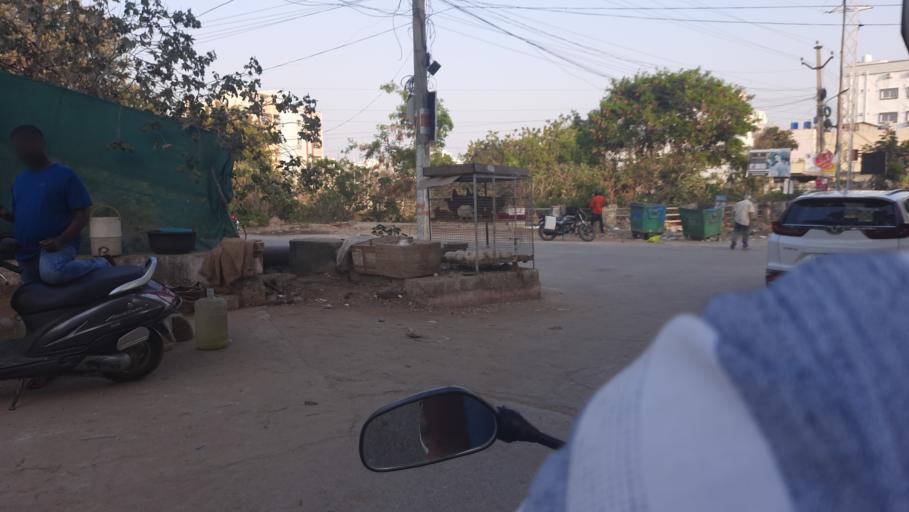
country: IN
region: Telangana
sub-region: Rangareddi
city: Secunderabad
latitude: 17.4966
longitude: 78.5433
